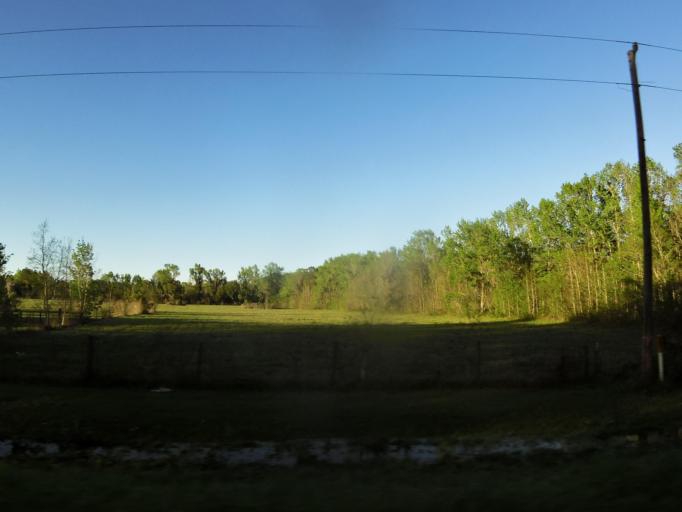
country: US
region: Florida
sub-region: Clay County
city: Keystone Heights
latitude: 29.8434
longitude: -82.0711
